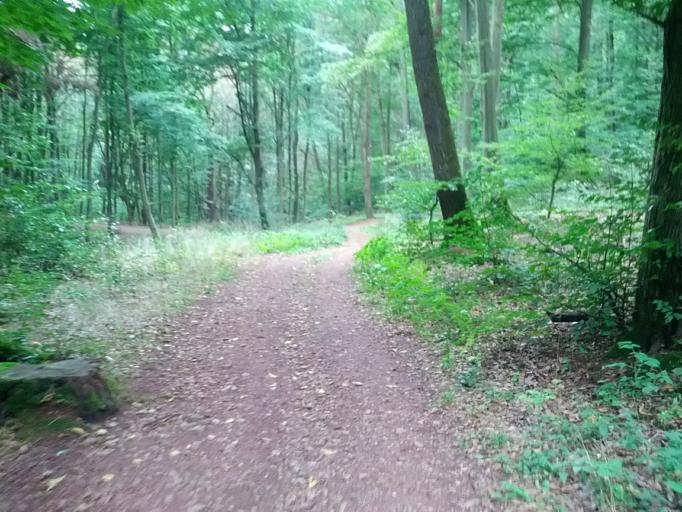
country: DE
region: Thuringia
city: Eisenach
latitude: 50.9551
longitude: 10.3053
